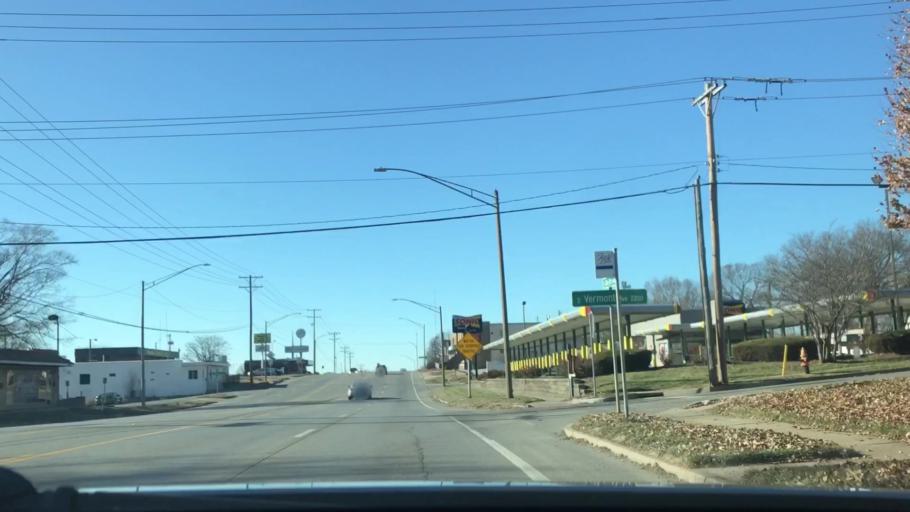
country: US
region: Missouri
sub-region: Jackson County
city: Independence
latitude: 39.0800
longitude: -94.4346
